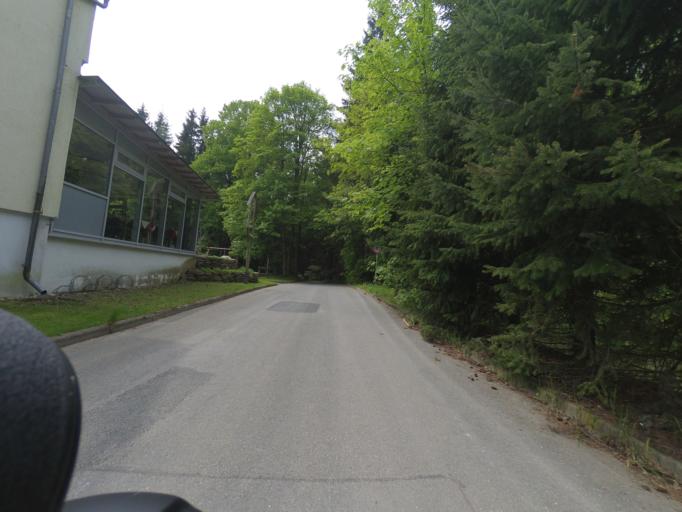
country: DE
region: Saxony
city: Grossruckerswalde
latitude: 50.6570
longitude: 13.1237
